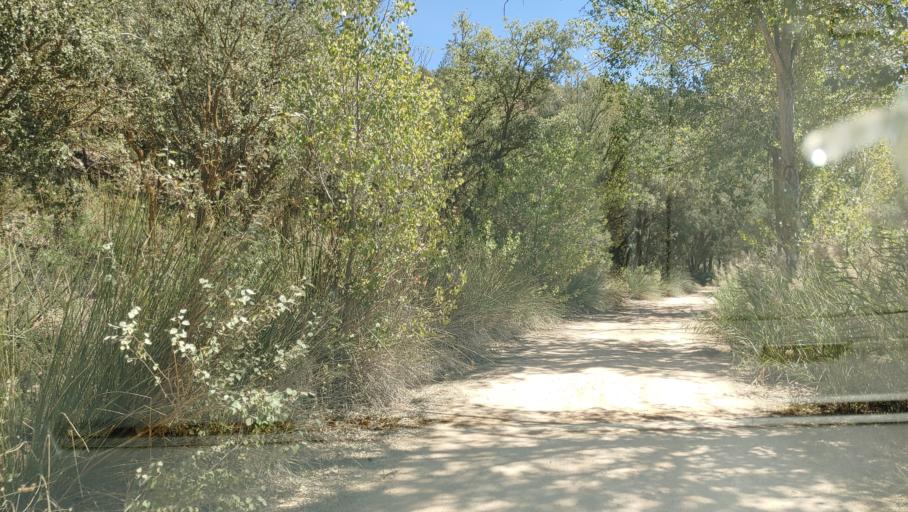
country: ES
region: Castille-La Mancha
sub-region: Provincia de Albacete
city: Ossa de Montiel
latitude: 38.9267
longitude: -2.8135
